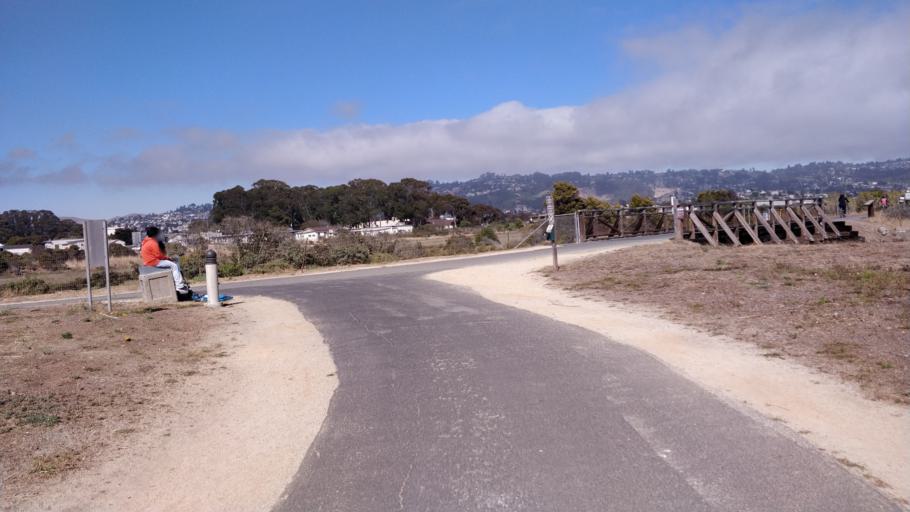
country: US
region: California
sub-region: Contra Costa County
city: El Cerrito
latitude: 37.9107
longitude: -122.3376
